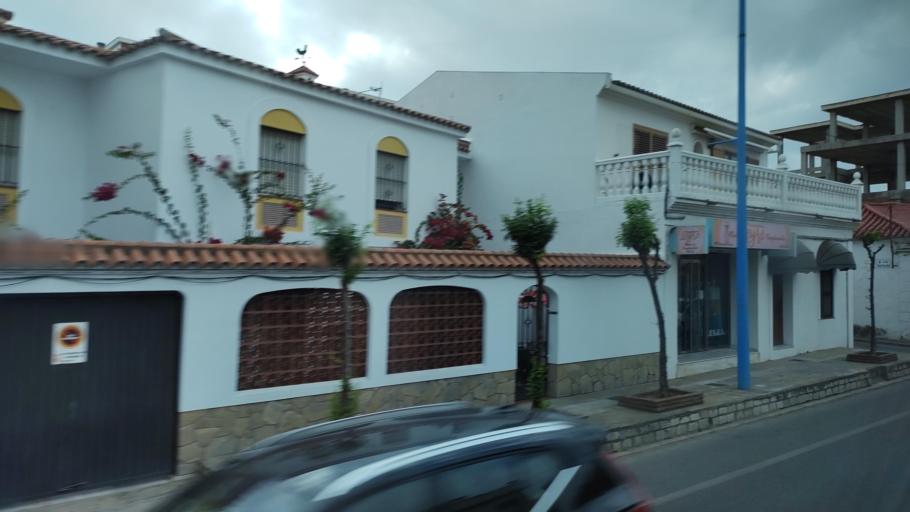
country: ES
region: Andalusia
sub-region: Provincia de Cadiz
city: San Roque
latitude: 36.1788
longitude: -5.3784
